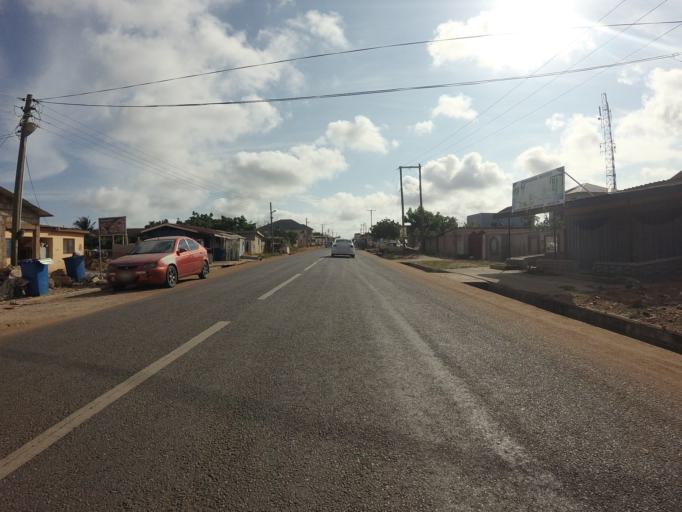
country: GH
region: Greater Accra
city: Teshi Old Town
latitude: 5.5886
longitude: -0.1371
